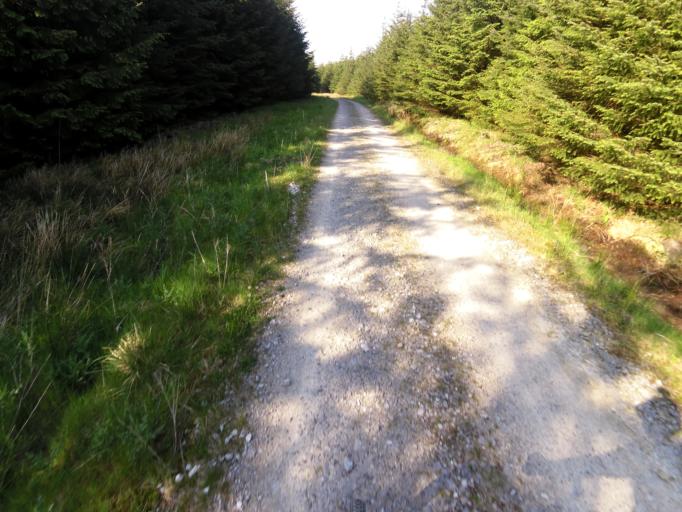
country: GB
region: England
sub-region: North Yorkshire
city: Settle
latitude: 54.0315
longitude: -2.3706
